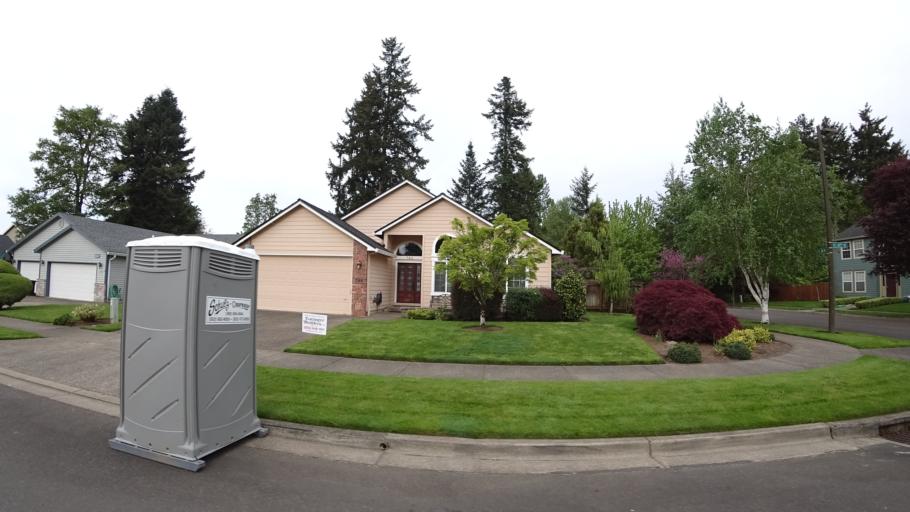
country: US
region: Oregon
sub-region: Washington County
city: Aloha
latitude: 45.5139
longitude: -122.9166
